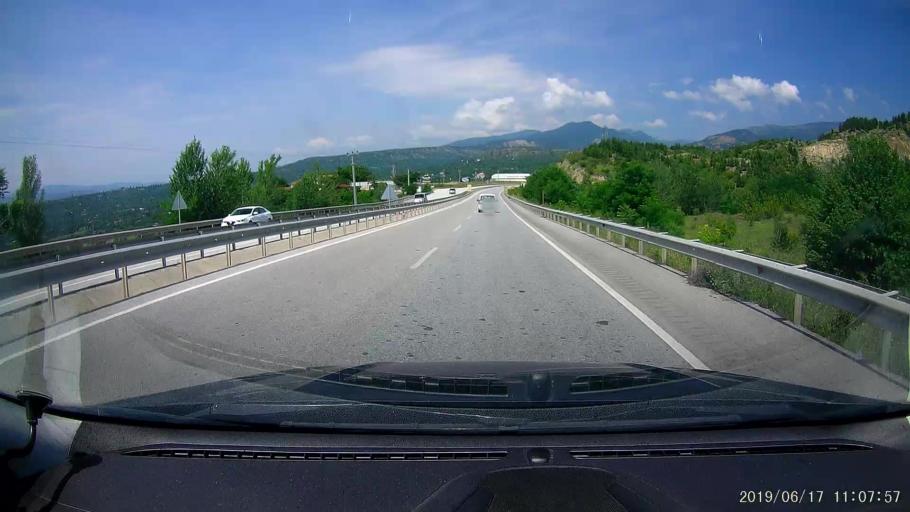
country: TR
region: Kastamonu
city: Tosya
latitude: 40.9995
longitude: 34.0463
